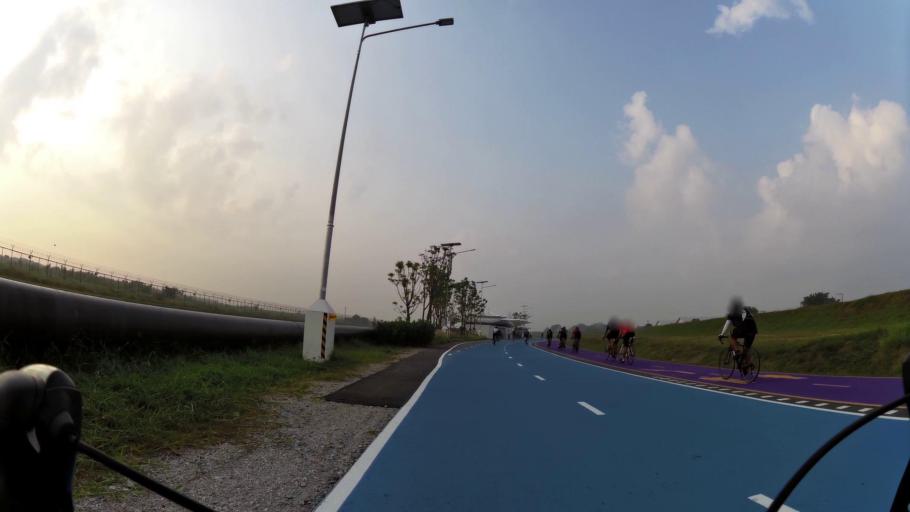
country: TH
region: Bangkok
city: Lat Krabang
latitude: 13.6828
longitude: 100.7669
